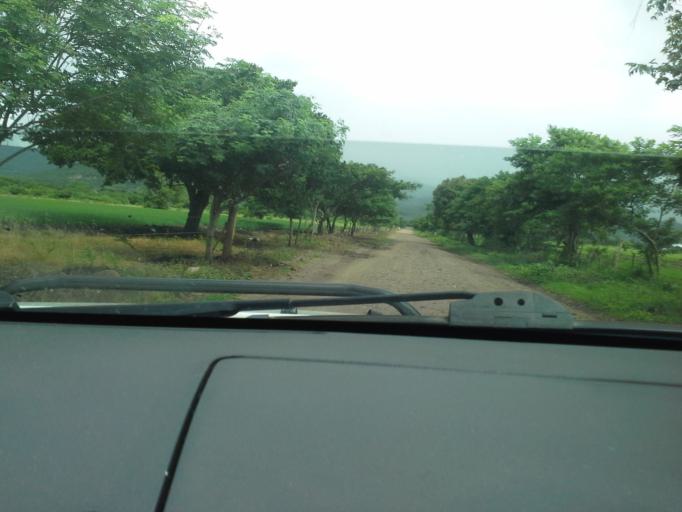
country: NI
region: Matagalpa
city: Ciudad Dario
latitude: 12.8648
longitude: -86.1925
